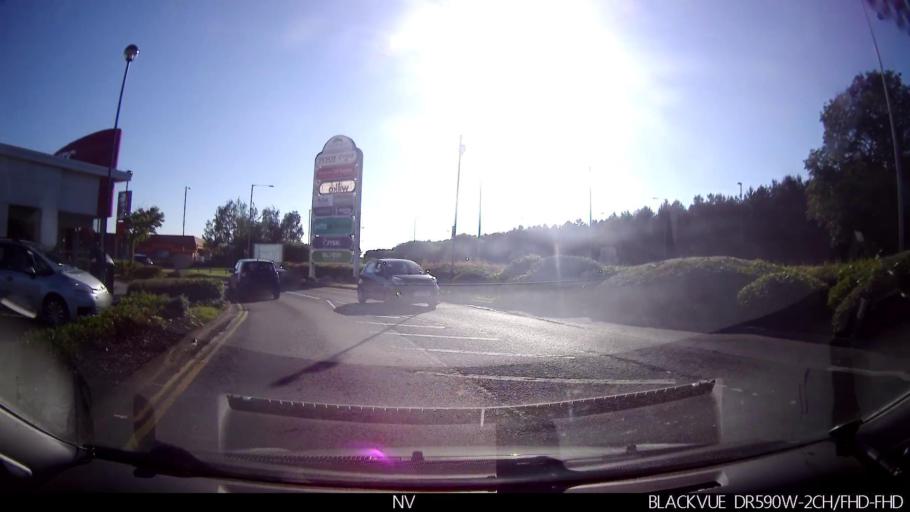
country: GB
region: England
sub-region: City of York
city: Skelton
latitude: 53.9931
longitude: -1.1060
